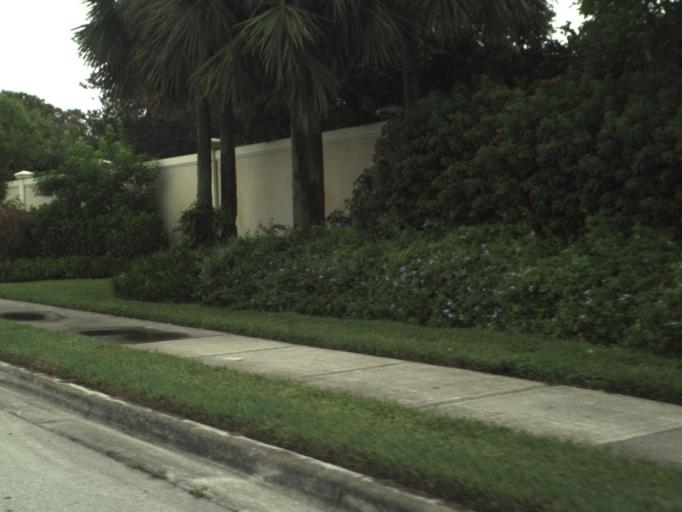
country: US
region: Florida
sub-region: Palm Beach County
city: Kings Point
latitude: 26.4485
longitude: -80.1223
